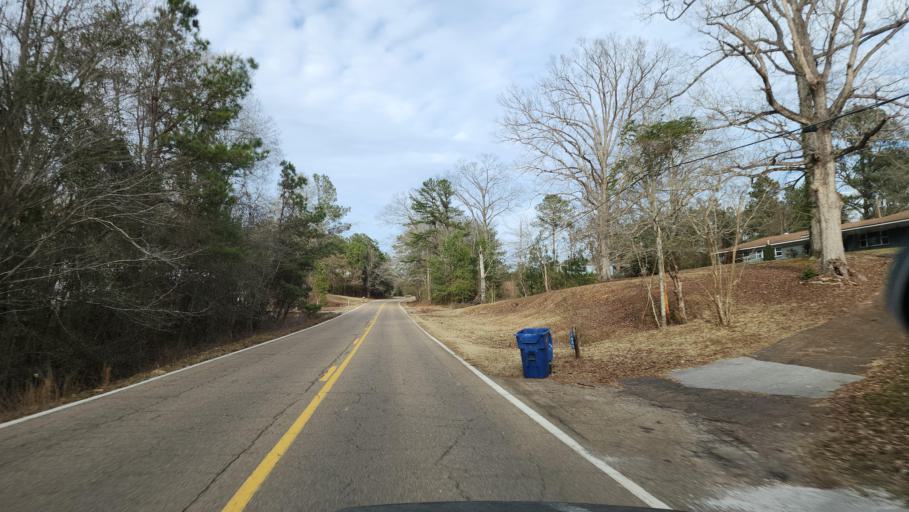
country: US
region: Mississippi
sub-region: Lauderdale County
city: Meridian
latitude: 32.2734
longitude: -88.7022
